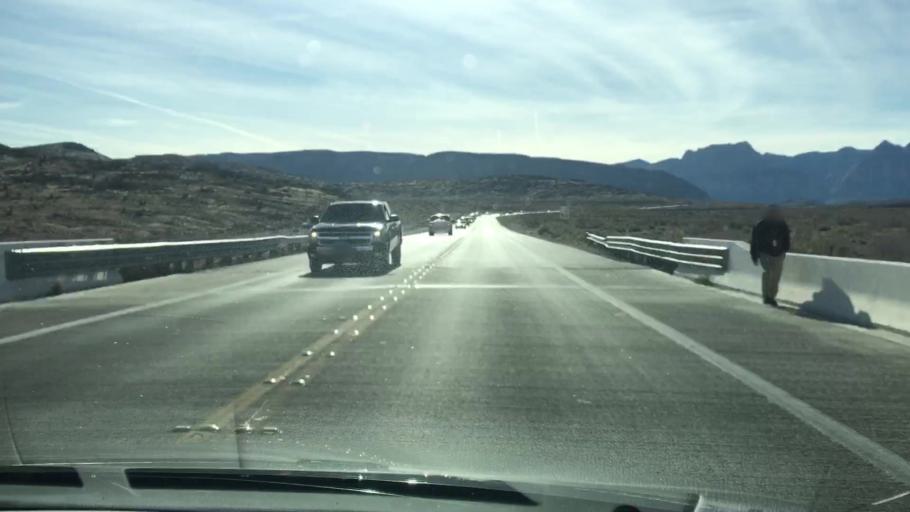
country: US
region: Nevada
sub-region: Clark County
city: Summerlin South
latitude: 36.1567
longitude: -115.3618
